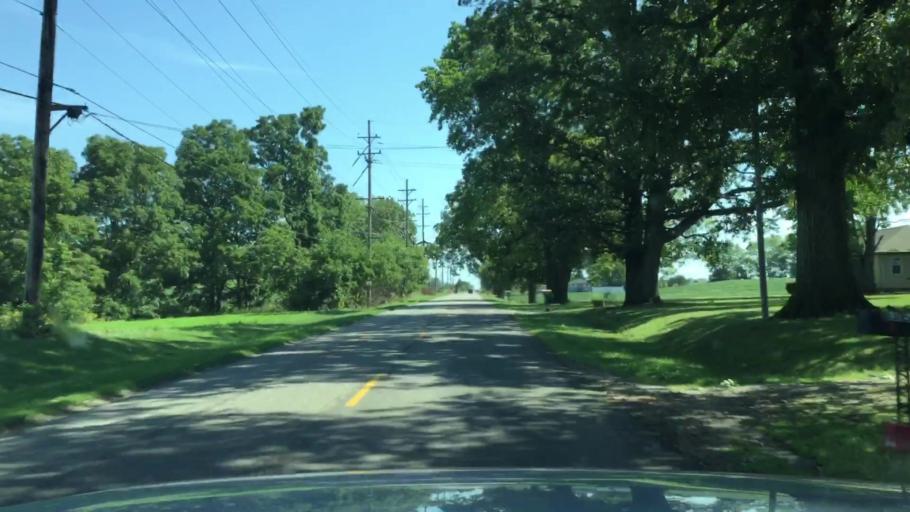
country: US
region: Michigan
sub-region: Lenawee County
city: Clinton
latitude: 42.0650
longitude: -83.9606
